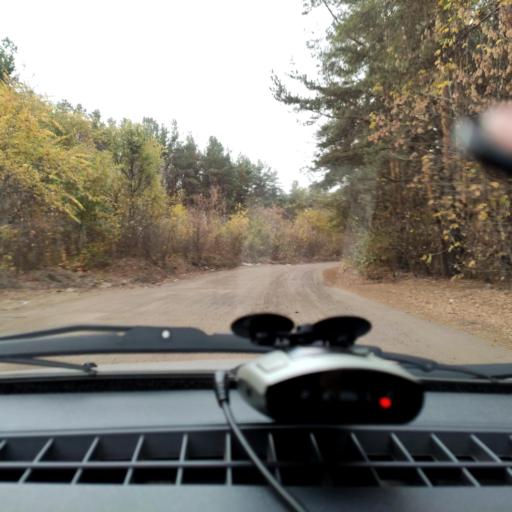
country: RU
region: Voronezj
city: Pridonskoy
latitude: 51.6748
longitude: 39.1251
